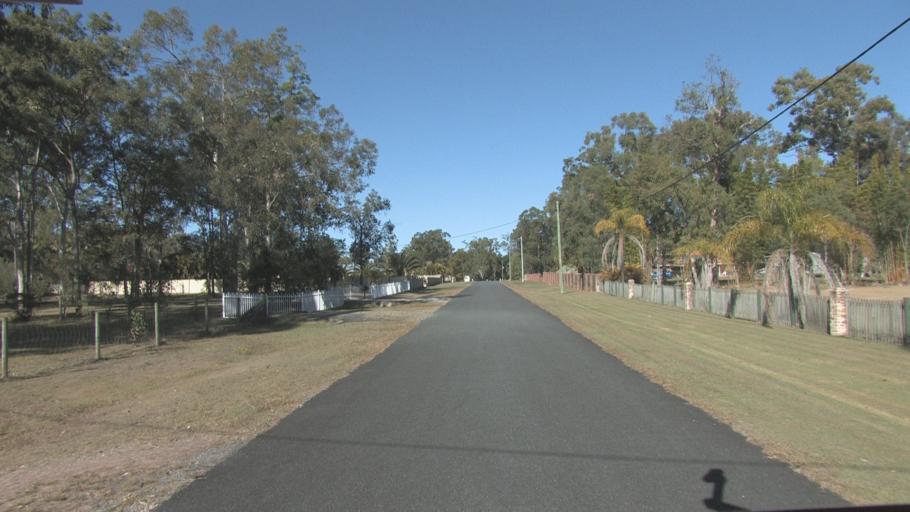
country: AU
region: Queensland
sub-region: Logan
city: Chambers Flat
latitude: -27.7495
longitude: 153.0511
